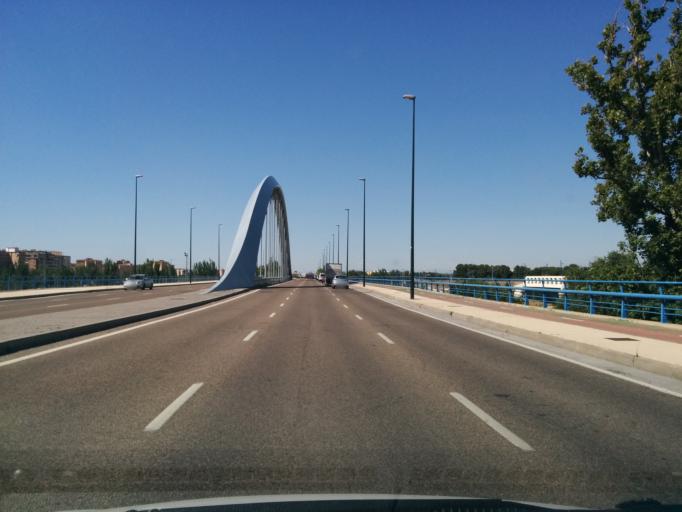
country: ES
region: Aragon
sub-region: Provincia de Zaragoza
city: Zaragoza
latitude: 41.6500
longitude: -0.8548
